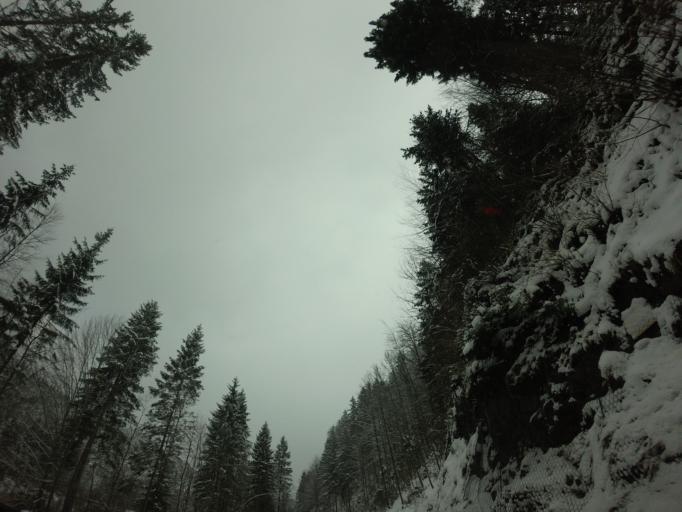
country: DE
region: Bavaria
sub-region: Upper Bavaria
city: Grainau
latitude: 47.4832
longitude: 11.0319
